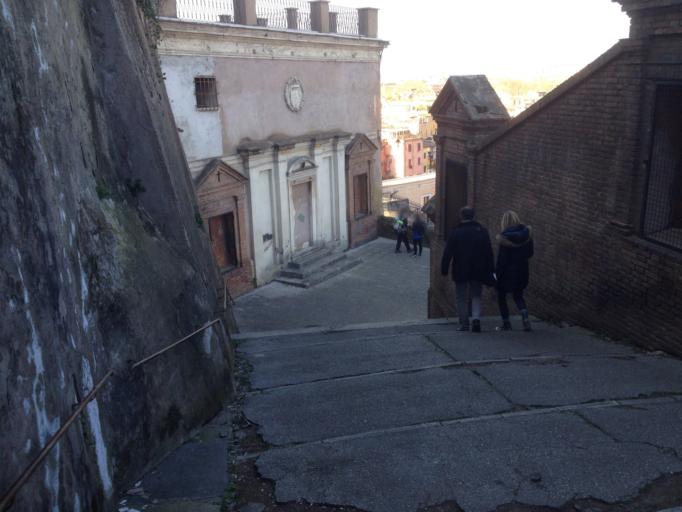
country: VA
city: Vatican City
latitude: 41.8890
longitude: 12.4666
